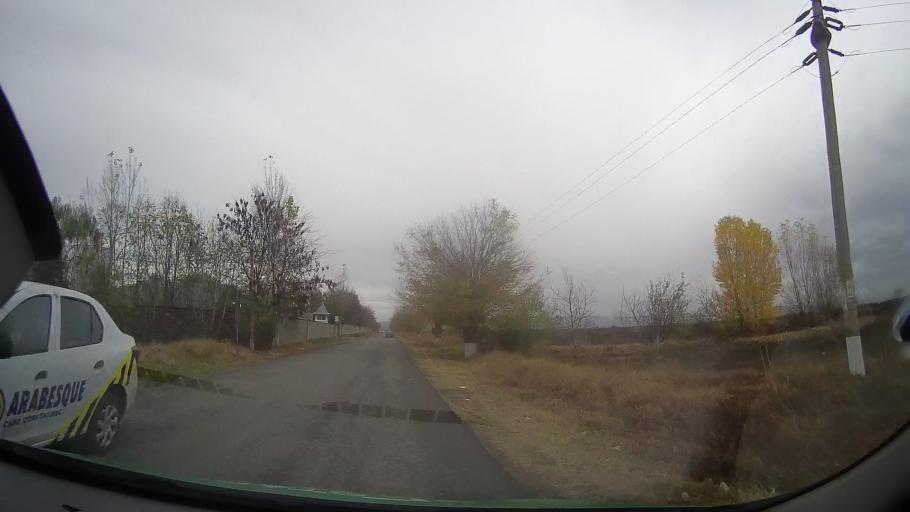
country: RO
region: Prahova
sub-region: Comuna Colceag
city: Inotesti
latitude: 44.9701
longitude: 26.3435
